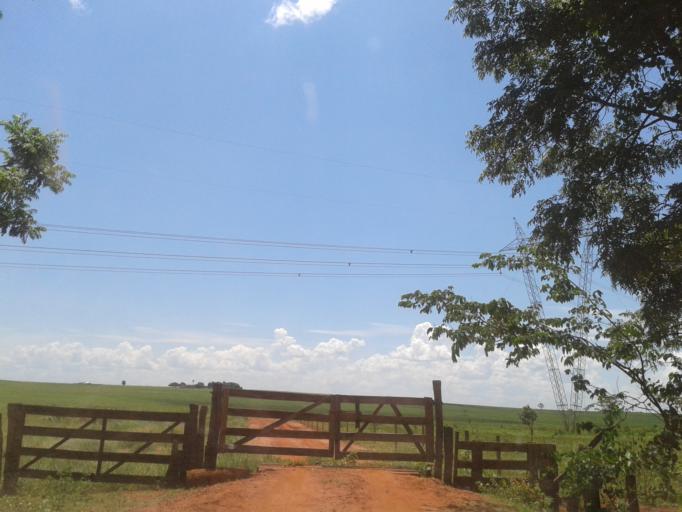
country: BR
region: Minas Gerais
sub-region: Santa Vitoria
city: Santa Vitoria
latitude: -19.1604
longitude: -50.4077
